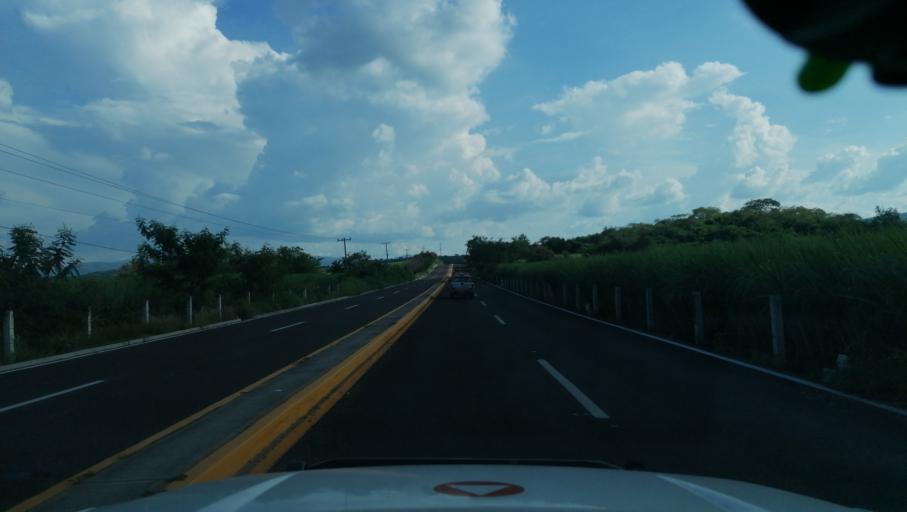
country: MX
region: Morelos
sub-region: Ayala
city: Abelardo L. Rodriguez
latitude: 18.7125
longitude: -98.9908
